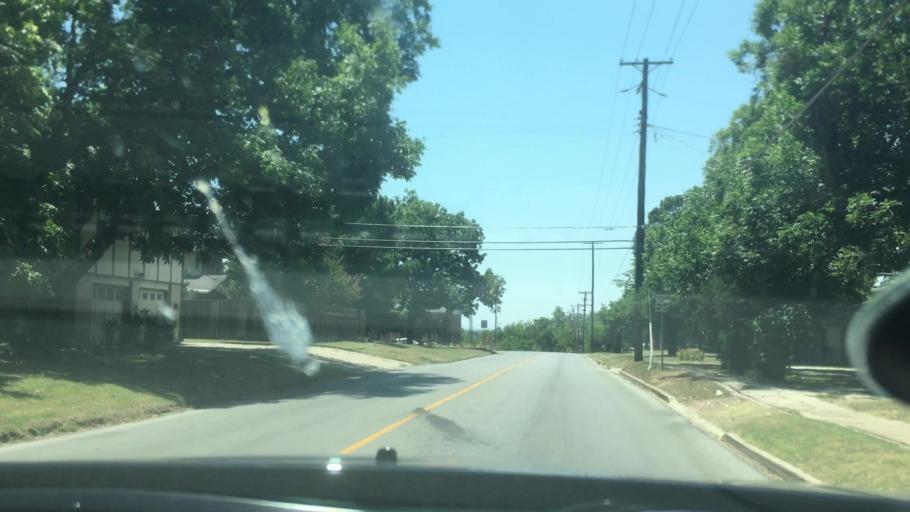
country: US
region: Oklahoma
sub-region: Pontotoc County
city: Ada
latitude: 34.7776
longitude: -96.6634
